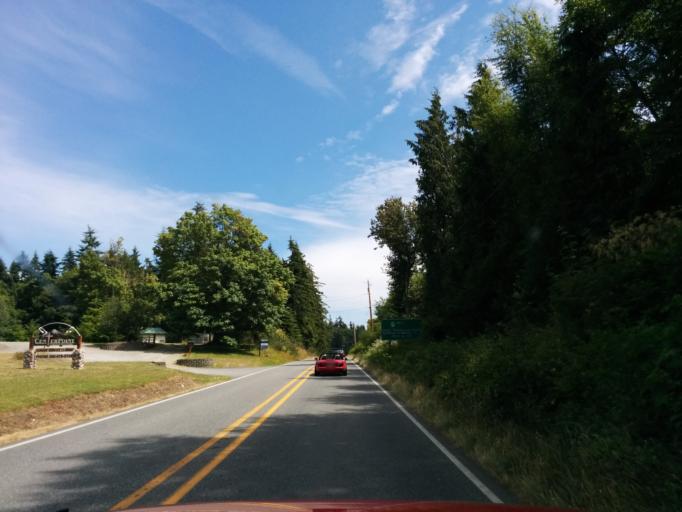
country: US
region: Washington
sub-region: Island County
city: Coupeville
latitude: 48.1742
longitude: -122.6143
